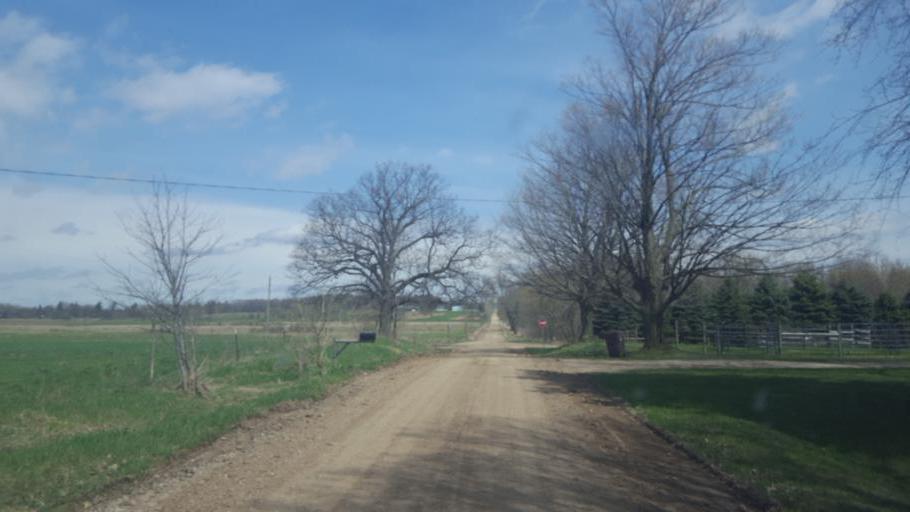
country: US
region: Michigan
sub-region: Montcalm County
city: Edmore
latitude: 43.4801
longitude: -84.9458
